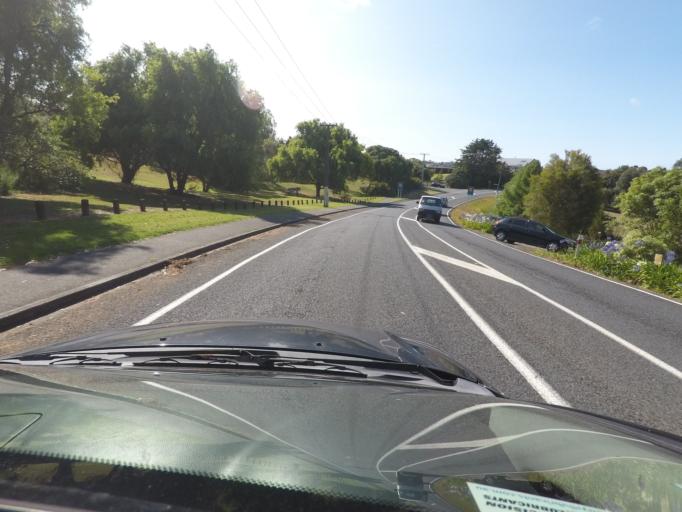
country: NZ
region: Auckland
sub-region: Auckland
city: Warkworth
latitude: -36.4294
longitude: 174.7372
